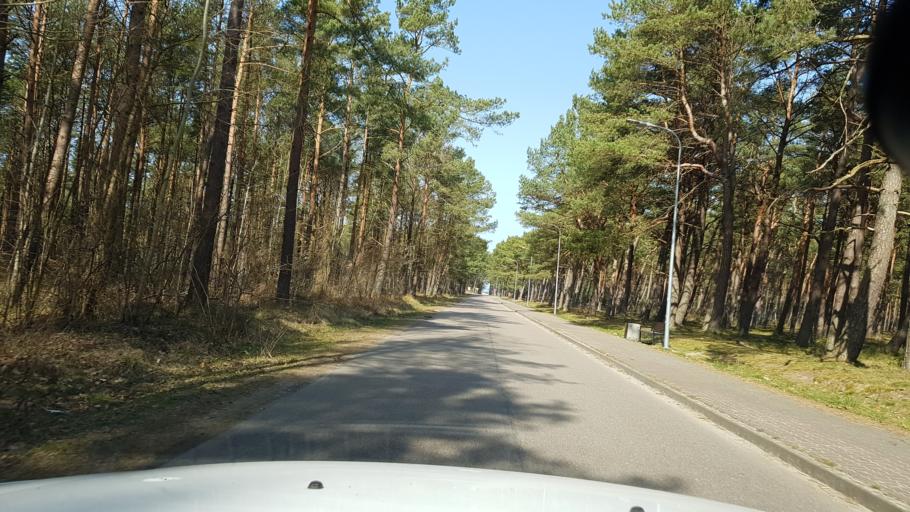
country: PL
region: West Pomeranian Voivodeship
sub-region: Powiat slawienski
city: Darlowo
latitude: 54.5238
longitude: 16.5109
